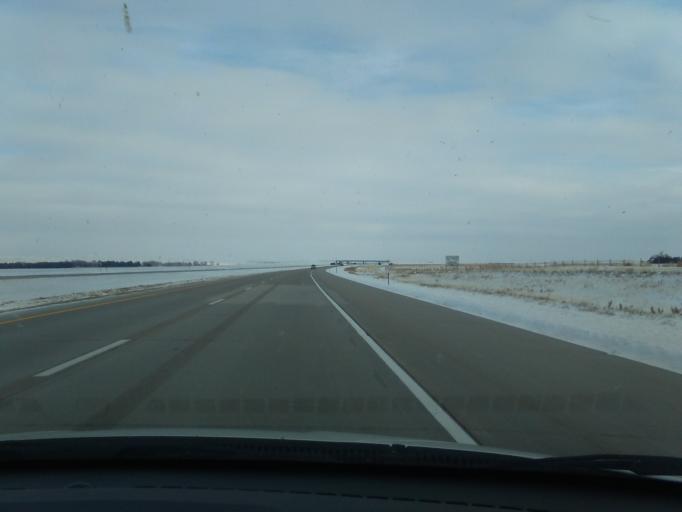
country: US
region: Nebraska
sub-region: Deuel County
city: Chappell
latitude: 41.1115
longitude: -102.5666
